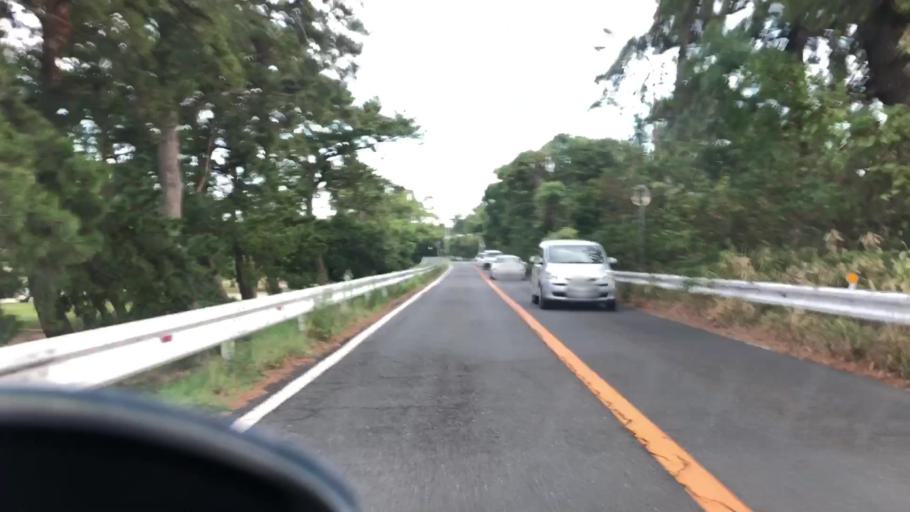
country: JP
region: Hyogo
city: Itami
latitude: 34.7550
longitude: 135.3724
